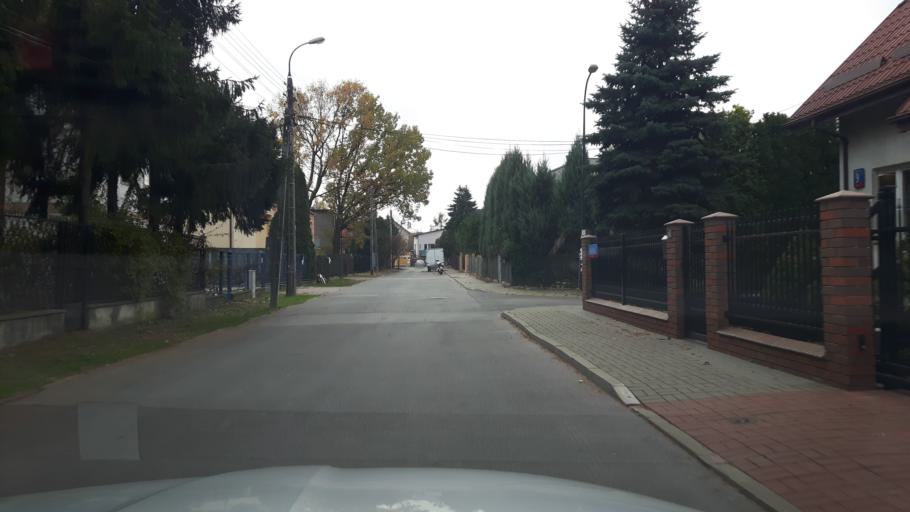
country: PL
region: Masovian Voivodeship
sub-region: Warszawa
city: Targowek
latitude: 52.2878
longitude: 21.0636
